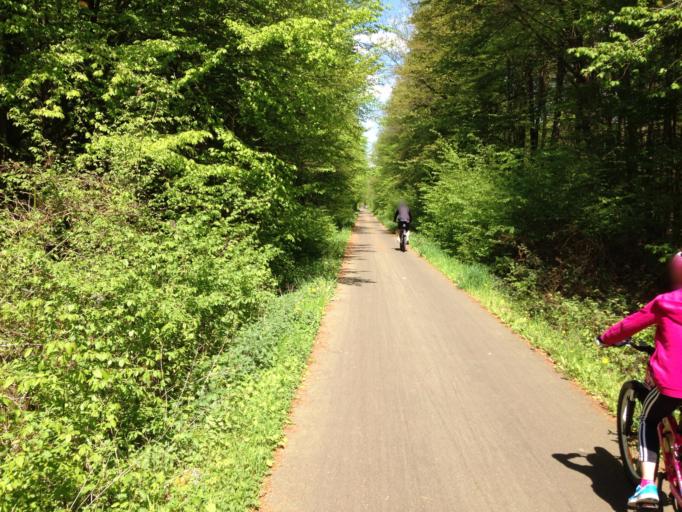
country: DE
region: Hesse
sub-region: Regierungsbezirk Giessen
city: Hungen
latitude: 50.4959
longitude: 8.9068
